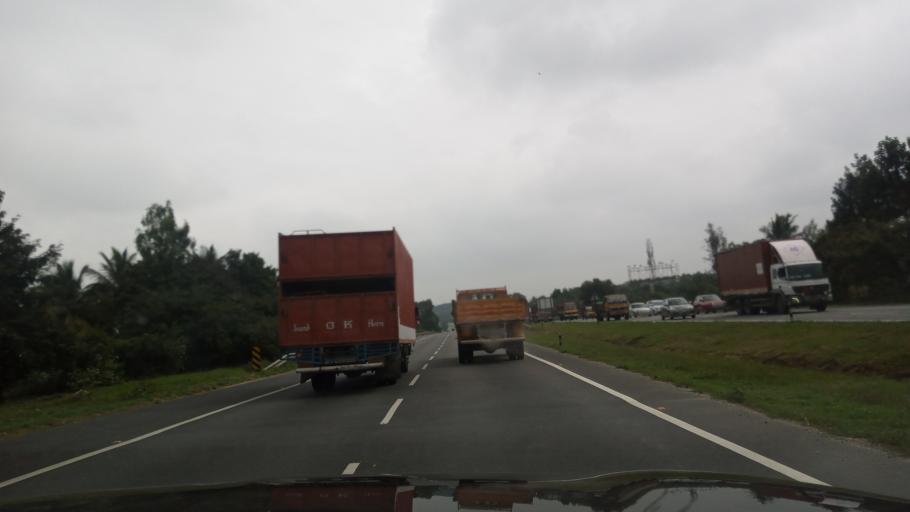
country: IN
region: Karnataka
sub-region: Bangalore Urban
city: Bangalore
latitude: 12.8535
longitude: 77.5961
